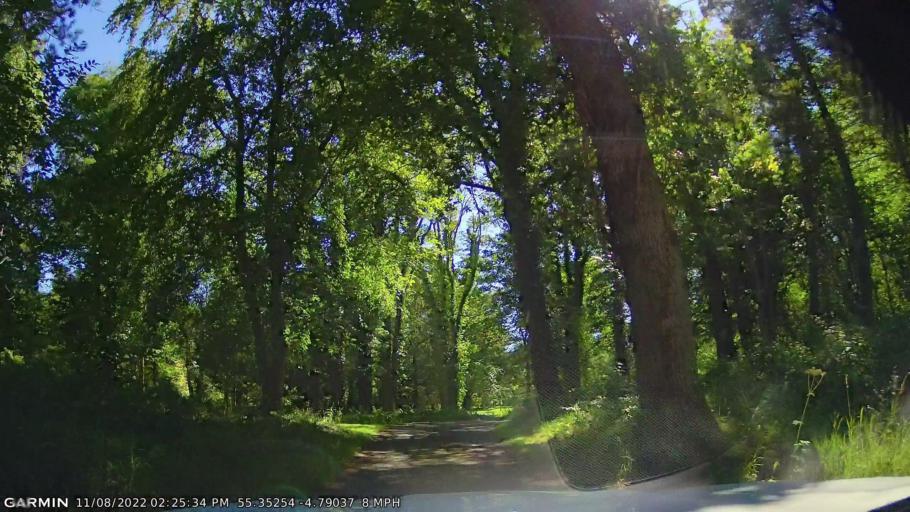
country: GB
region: Scotland
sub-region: South Ayrshire
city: Maybole
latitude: 55.3525
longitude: -4.7904
